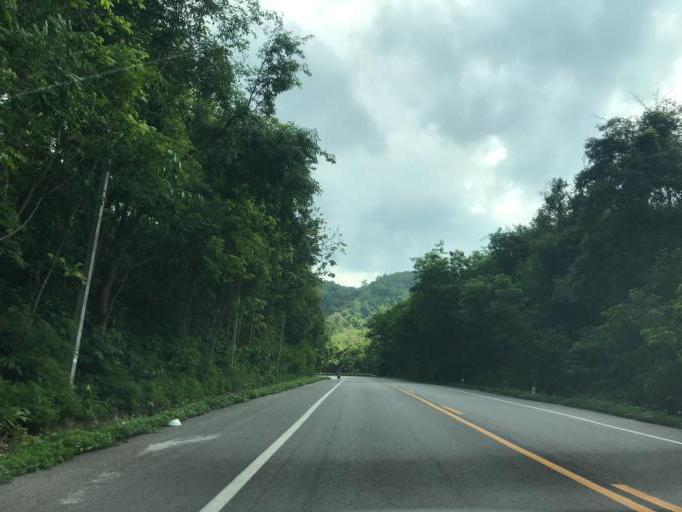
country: TH
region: Phayao
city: Phayao
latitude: 19.0875
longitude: 99.8206
